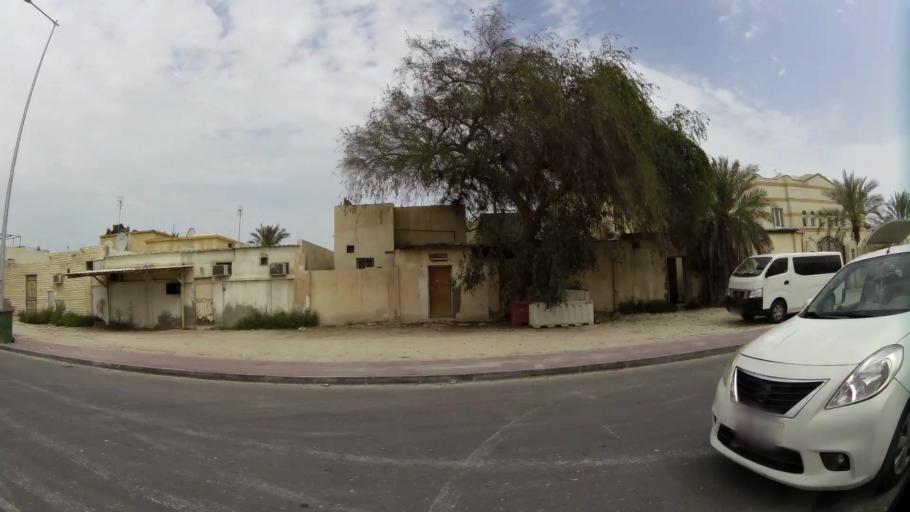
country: QA
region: Baladiyat ar Rayyan
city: Ar Rayyan
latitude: 25.3283
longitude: 51.4688
